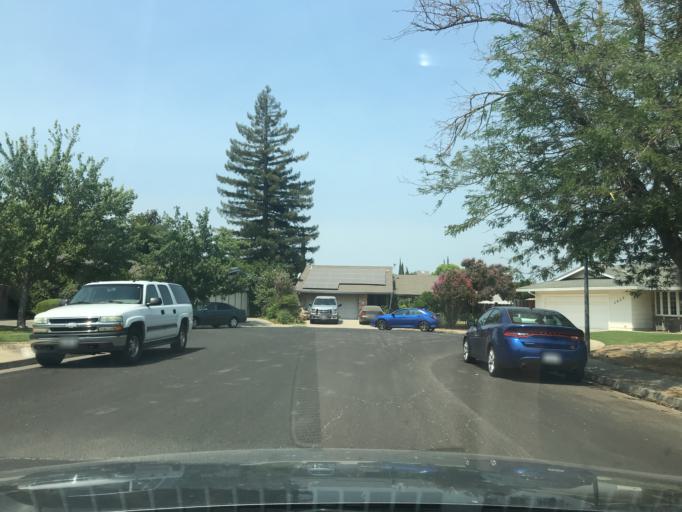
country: US
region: California
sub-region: Merced County
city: Merced
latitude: 37.3161
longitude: -120.4808
